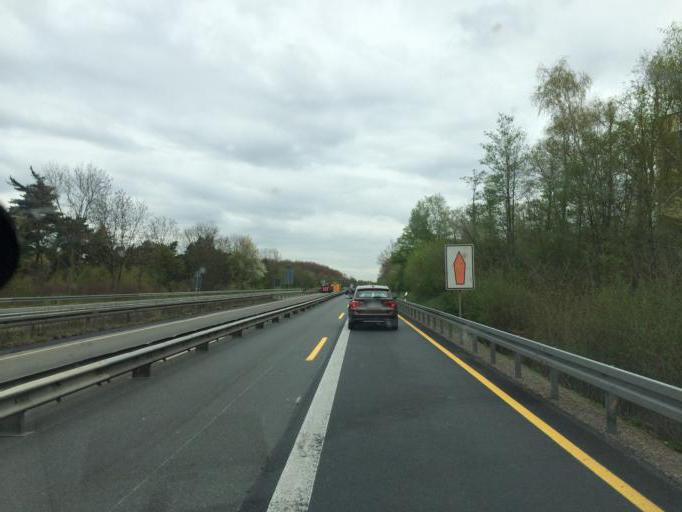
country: DE
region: North Rhine-Westphalia
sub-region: Regierungsbezirk Munster
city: Haltern
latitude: 51.6878
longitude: 7.1522
